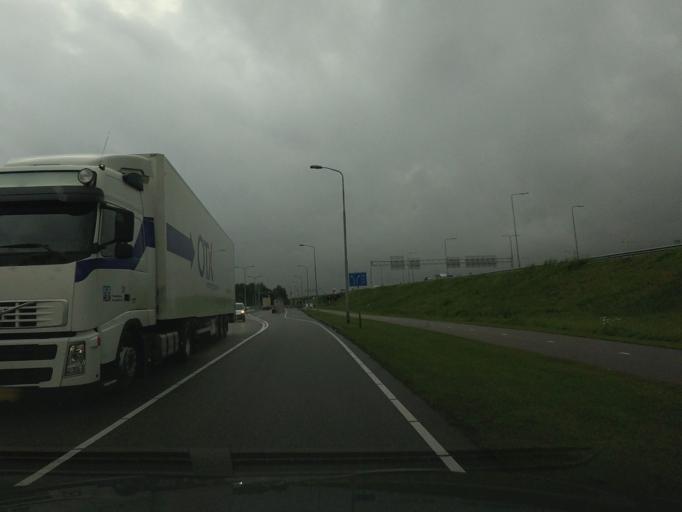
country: NL
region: North Holland
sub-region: Gemeente Aalsmeer
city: Aalsmeer
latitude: 52.2886
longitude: 4.7294
